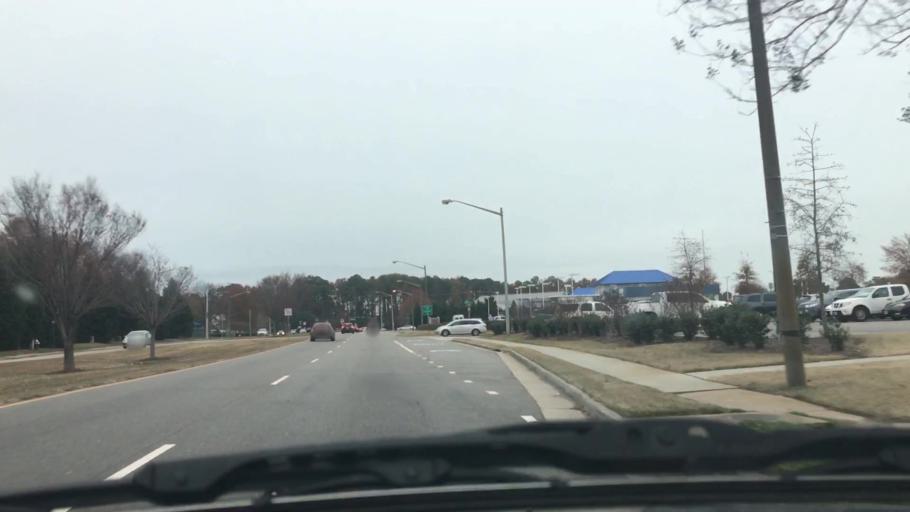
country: US
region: Virginia
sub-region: City of Chesapeake
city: Chesapeake
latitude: 36.8199
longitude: -76.1268
